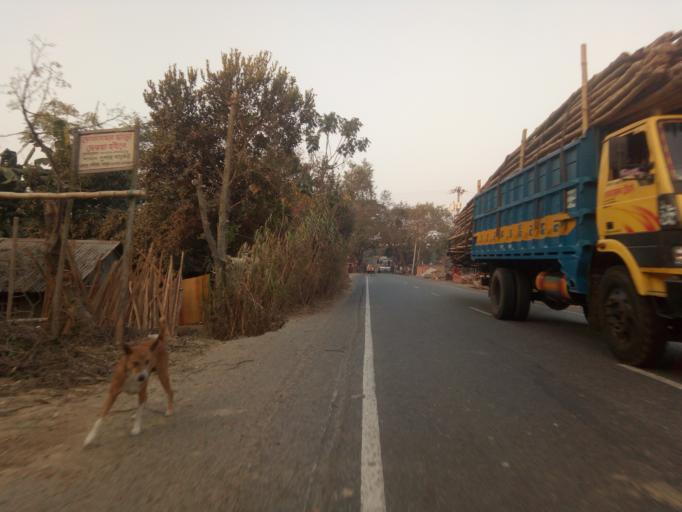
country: BD
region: Rajshahi
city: Bogra
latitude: 24.6263
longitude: 89.2431
